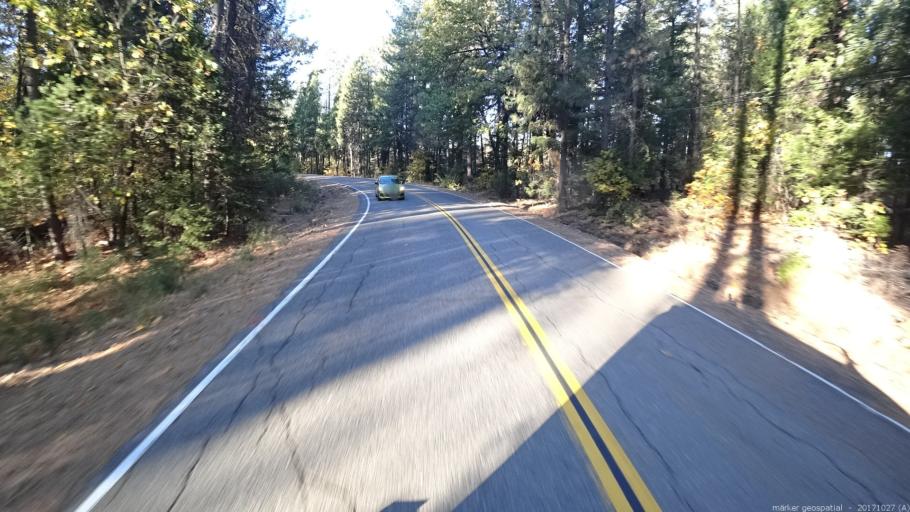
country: US
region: California
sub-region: Shasta County
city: Burney
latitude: 40.9981
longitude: -121.9192
